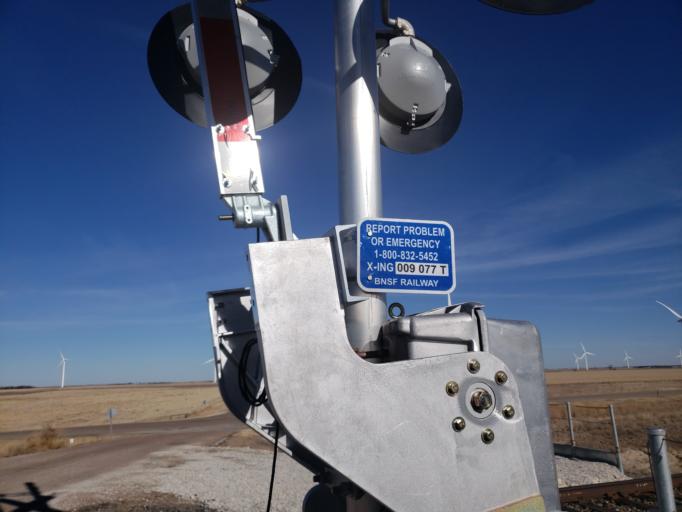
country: US
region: Kansas
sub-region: Edwards County
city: Kinsley
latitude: 37.8750
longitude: -99.6435
